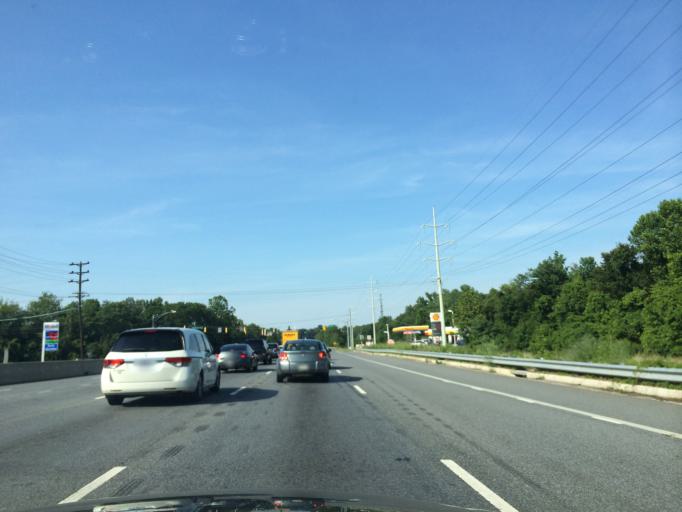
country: US
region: Maryland
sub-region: Anne Arundel County
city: Crofton
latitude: 38.9845
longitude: -76.7099
